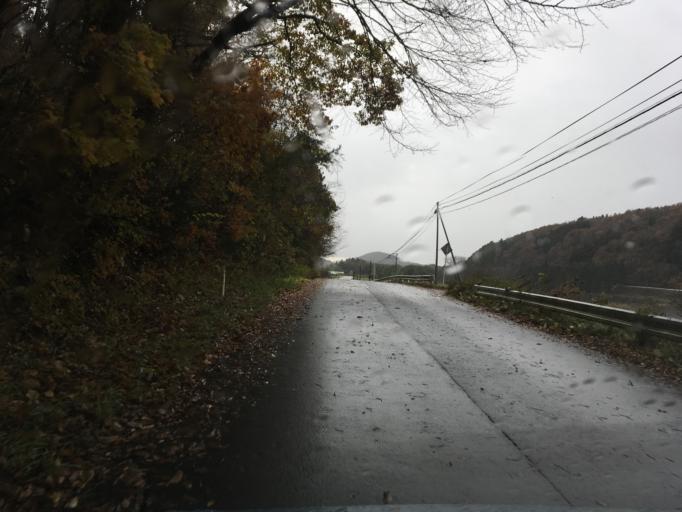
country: JP
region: Iwate
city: Ichinoseki
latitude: 38.8061
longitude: 141.2500
